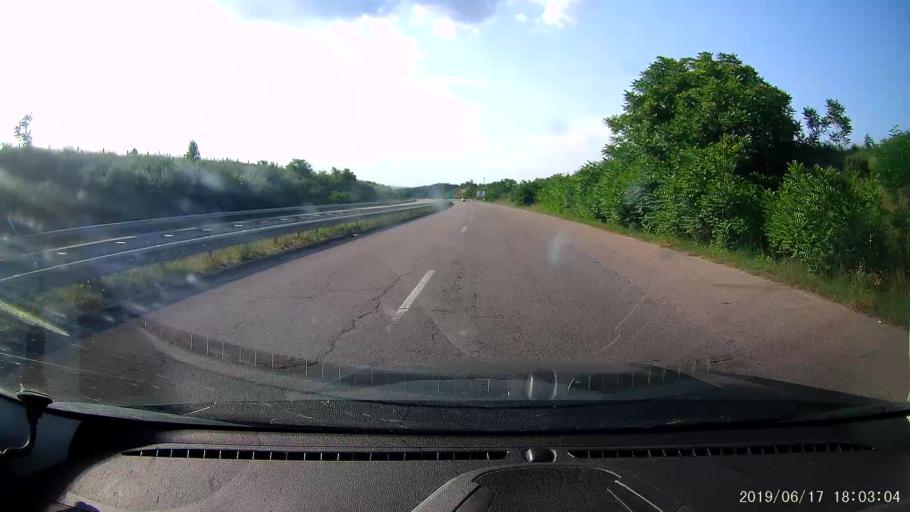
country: BG
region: Khaskovo
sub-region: Obshtina Svilengrad
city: Svilengrad
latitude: 41.7716
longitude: 26.2245
